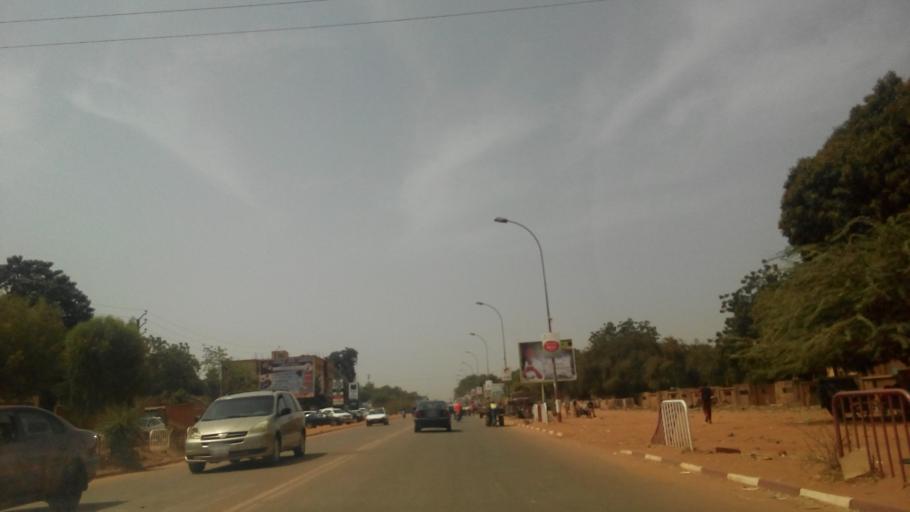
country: NE
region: Niamey
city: Niamey
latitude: 13.5242
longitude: 2.1009
